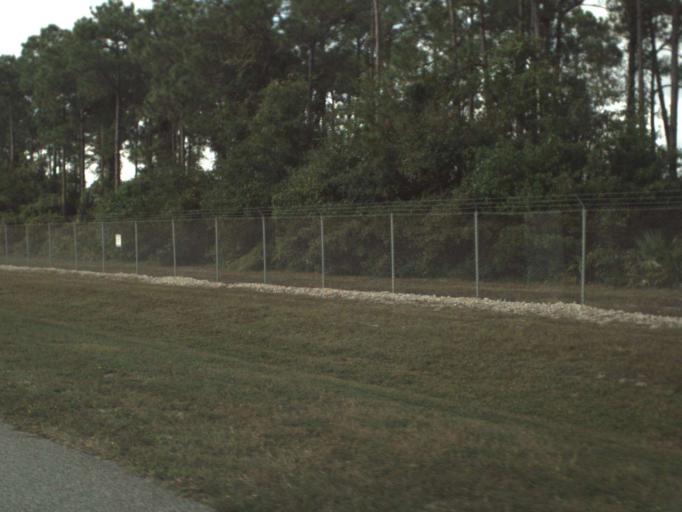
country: US
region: Florida
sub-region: Bay County
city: Tyndall Air Force Base
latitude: 30.0564
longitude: -85.5726
